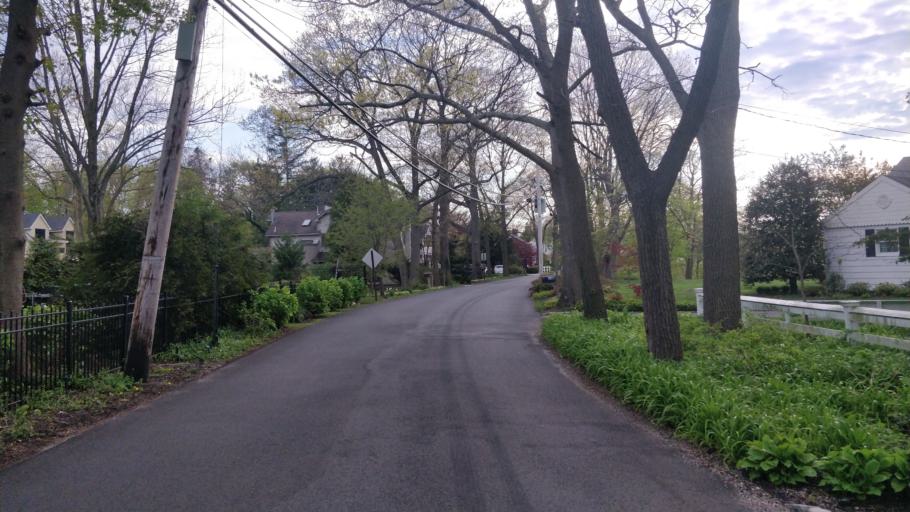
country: US
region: New York
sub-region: Suffolk County
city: Northport
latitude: 40.9082
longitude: -73.3447
